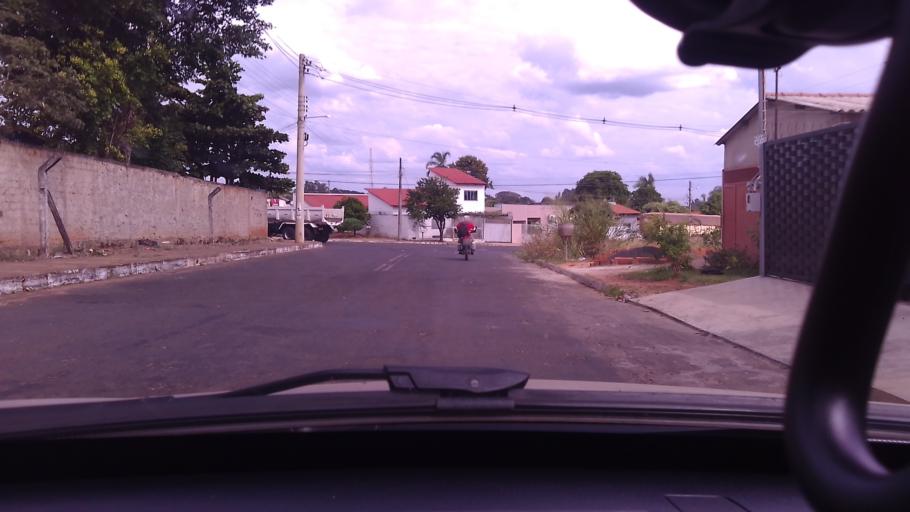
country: BR
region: Goias
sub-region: Mineiros
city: Mineiros
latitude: -17.5741
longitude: -52.5423
